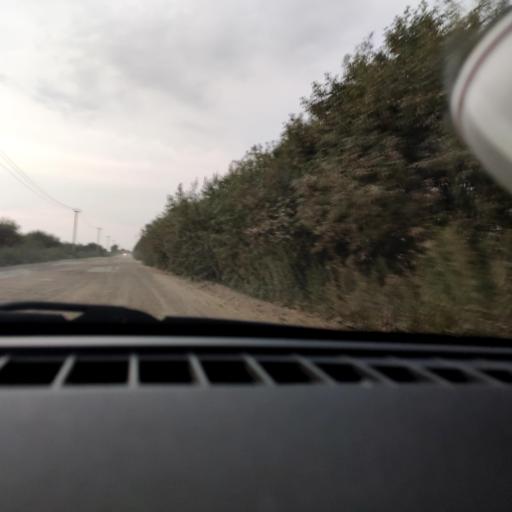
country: RU
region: Perm
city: Kondratovo
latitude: 58.0033
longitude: 56.0232
